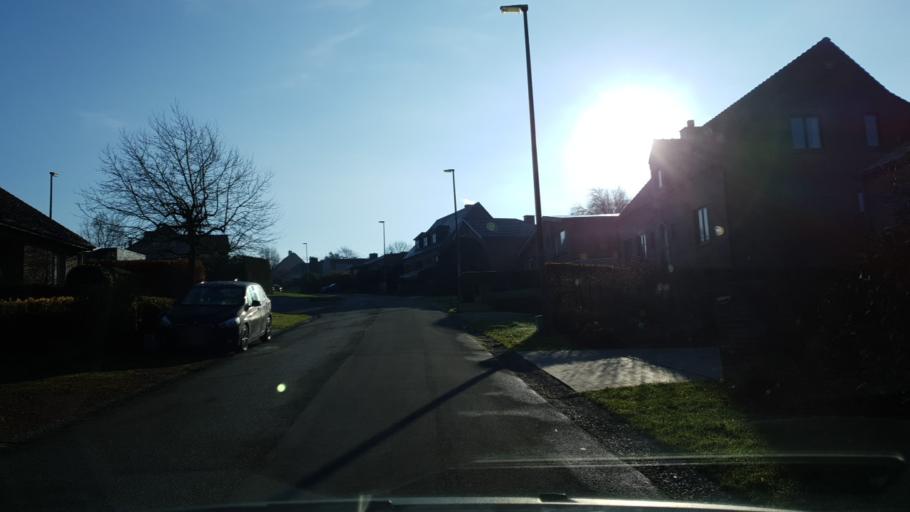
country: BE
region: Flanders
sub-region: Provincie Vlaams-Brabant
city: Herent
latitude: 50.8832
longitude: 4.6642
